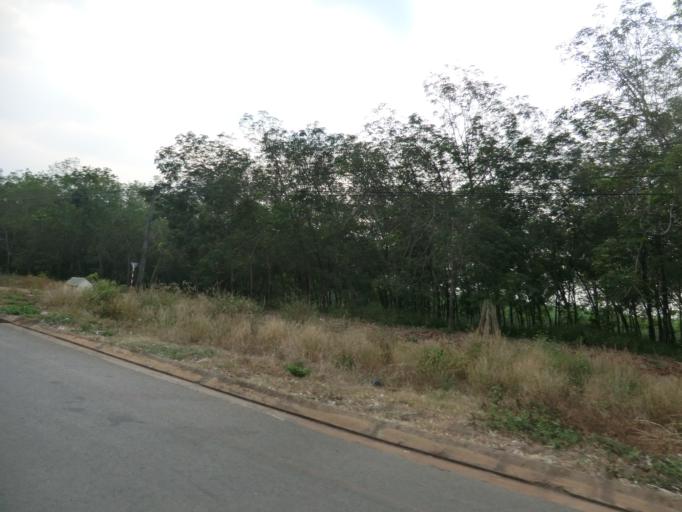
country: VN
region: Dong Nai
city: Thong Nhat
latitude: 10.9698
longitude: 107.1443
